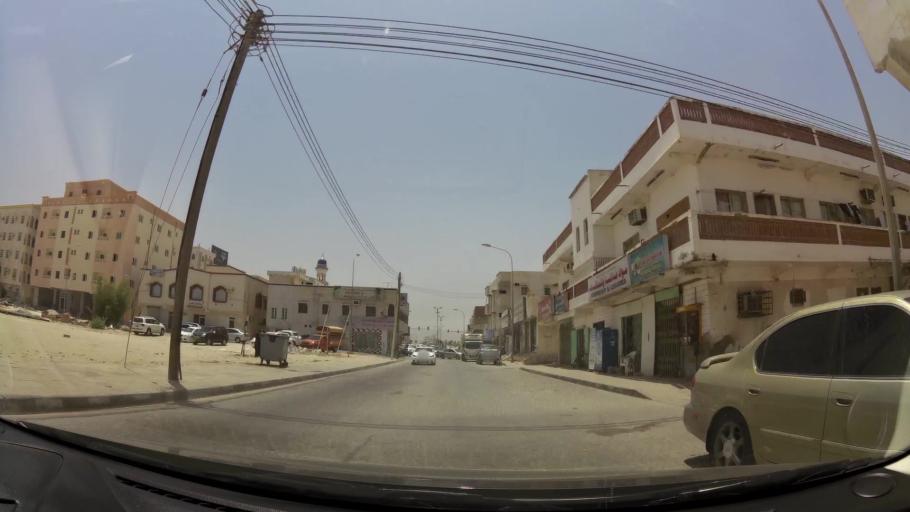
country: OM
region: Zufar
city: Salalah
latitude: 17.0163
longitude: 54.1013
